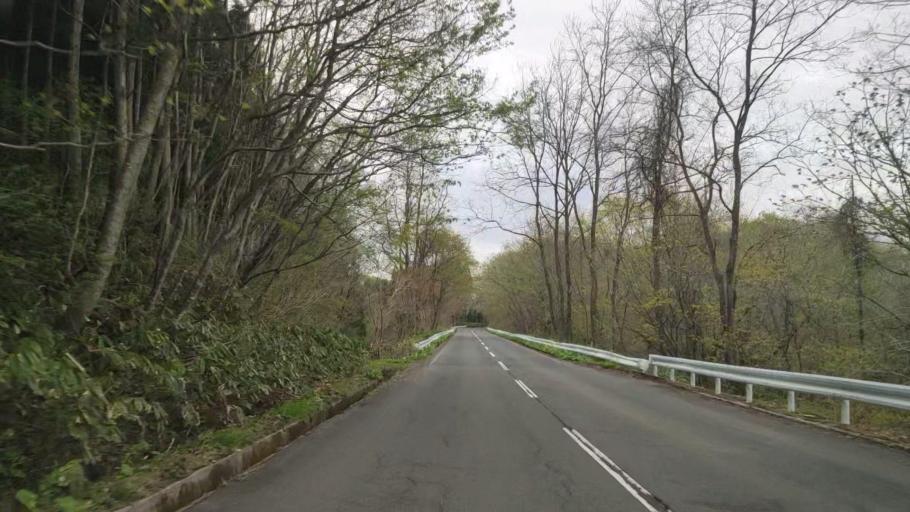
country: JP
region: Akita
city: Hanawa
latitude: 40.3813
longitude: 140.7907
